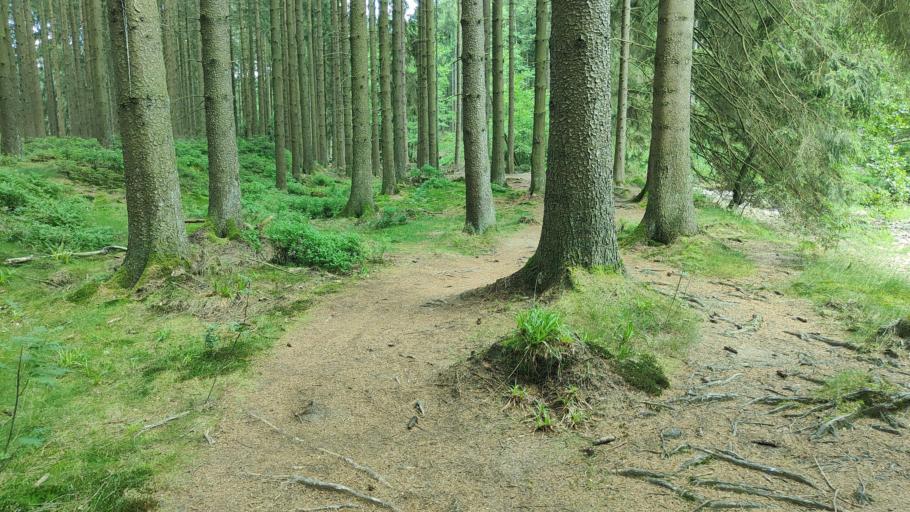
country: DE
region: North Rhine-Westphalia
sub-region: Regierungsbezirk Koln
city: Roetgen
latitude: 50.6320
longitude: 6.1566
